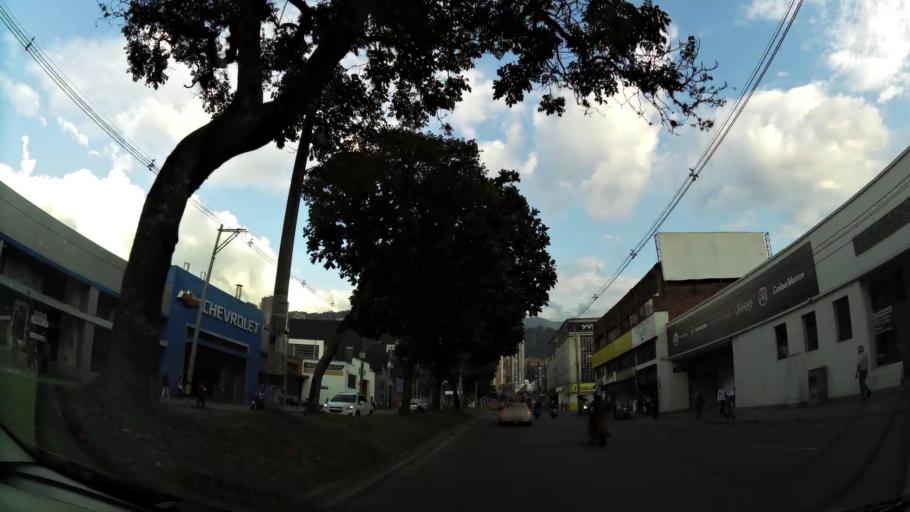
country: CO
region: Antioquia
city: Medellin
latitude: 6.2297
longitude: -75.5724
